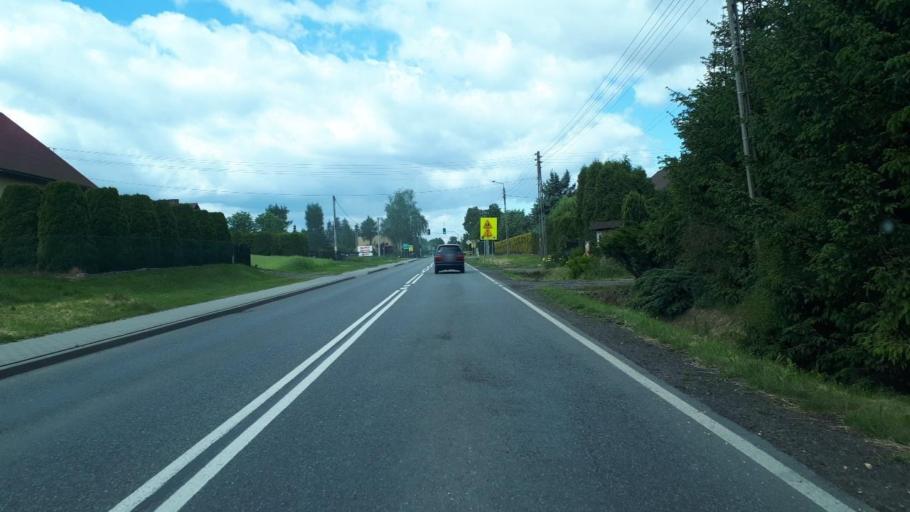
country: PL
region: Silesian Voivodeship
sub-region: Powiat pszczynski
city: Gora
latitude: 49.9727
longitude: 19.1043
